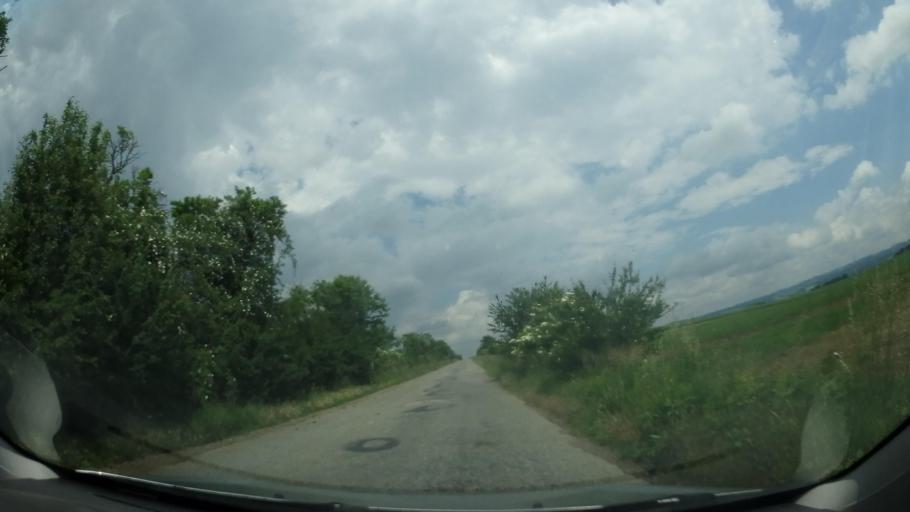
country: CZ
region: South Moravian
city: Boritov
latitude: 49.4335
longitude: 16.5939
